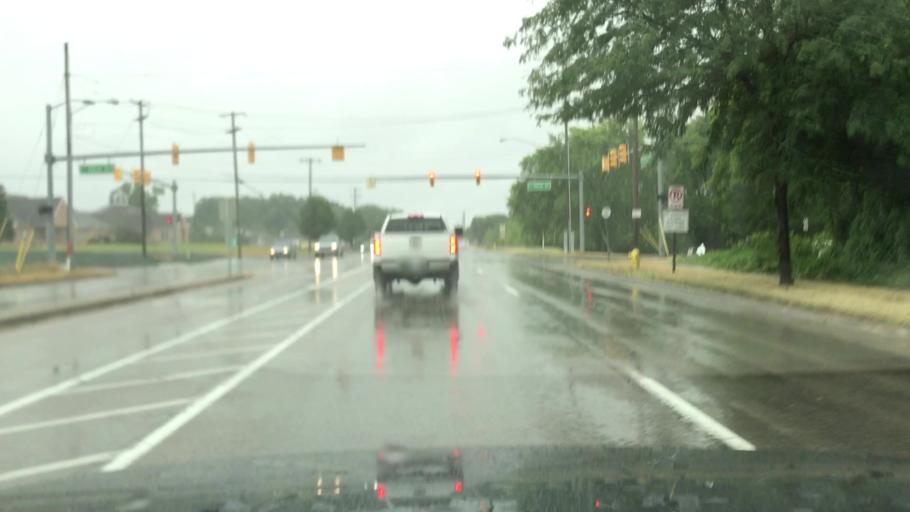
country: US
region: Michigan
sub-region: Kent County
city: Wyoming
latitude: 42.8706
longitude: -85.7235
